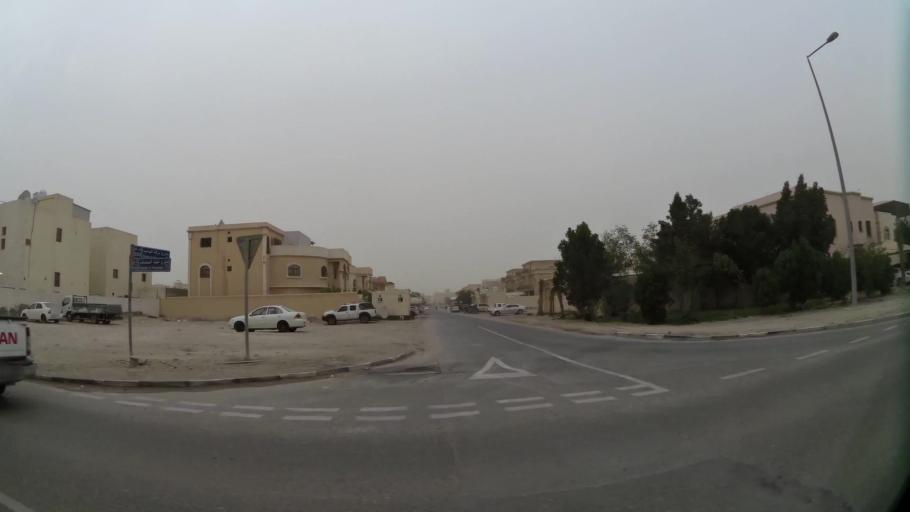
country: QA
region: Baladiyat ad Dawhah
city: Doha
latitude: 25.2417
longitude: 51.4872
